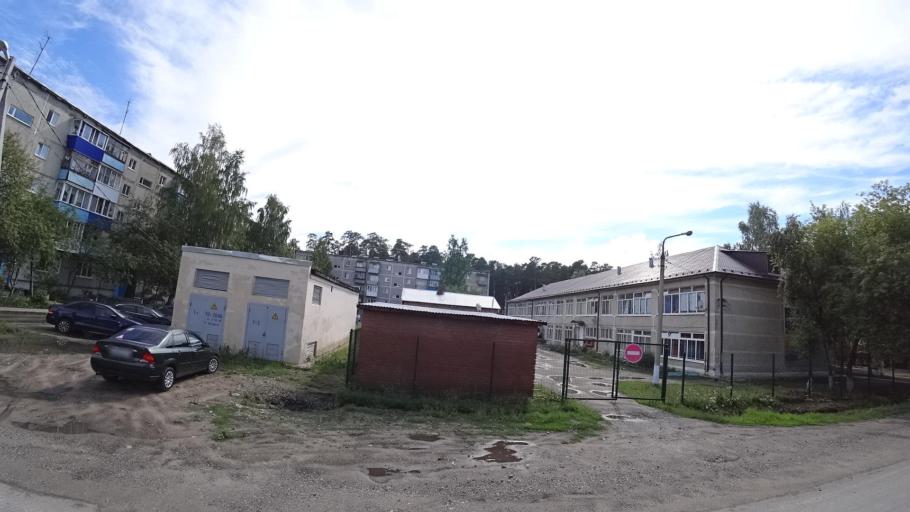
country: RU
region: Sverdlovsk
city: Kamyshlov
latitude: 56.8350
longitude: 62.7337
